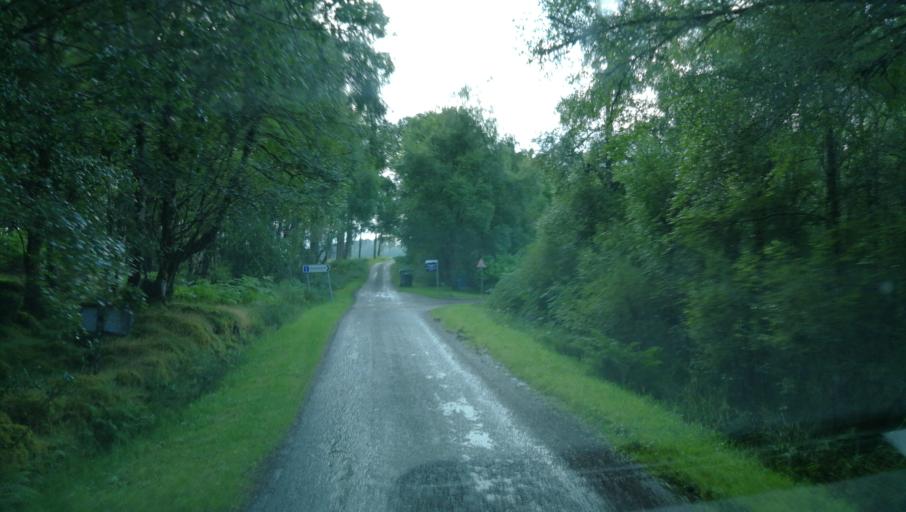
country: GB
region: Scotland
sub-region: Highland
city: Spean Bridge
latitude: 57.0698
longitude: -4.8261
